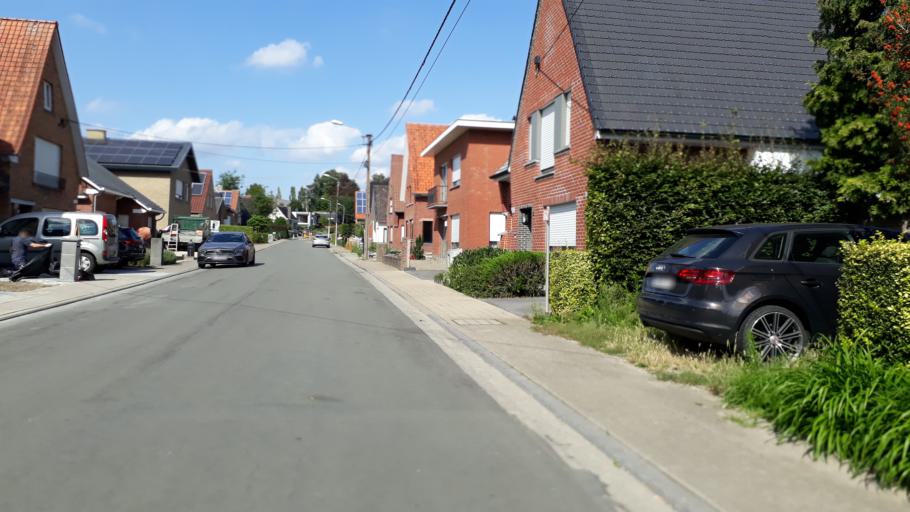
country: BE
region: Flanders
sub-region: Provincie West-Vlaanderen
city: Torhout
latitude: 51.0738
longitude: 3.0880
